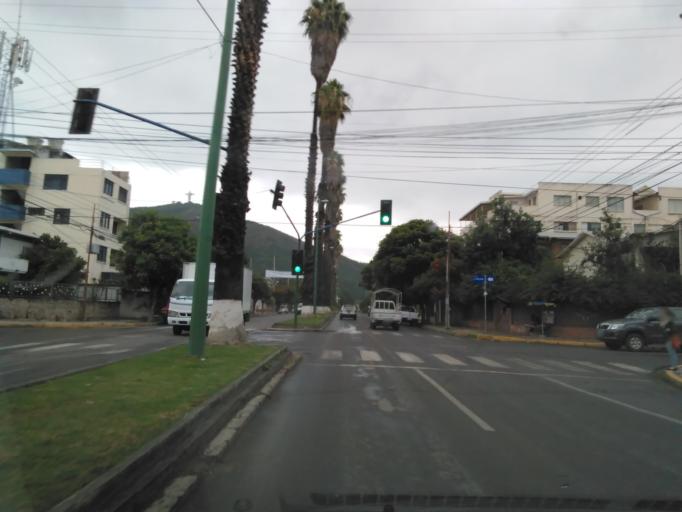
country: BO
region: Cochabamba
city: Cochabamba
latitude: -17.3907
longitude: -66.1481
